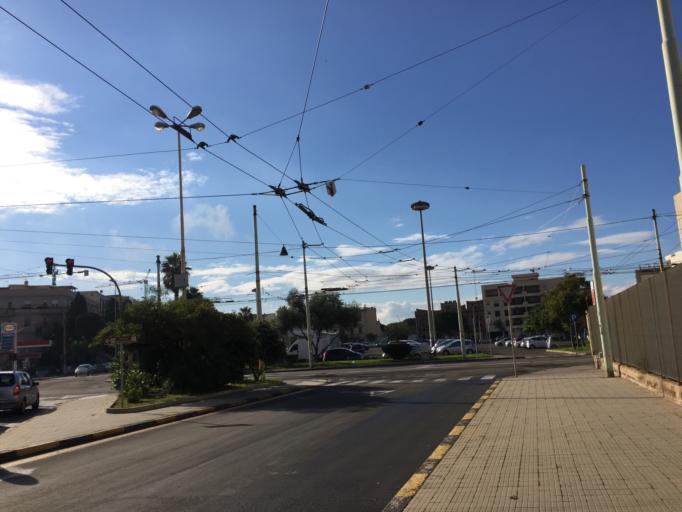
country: IT
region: Sardinia
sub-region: Provincia di Cagliari
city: Cagliari
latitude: 39.2103
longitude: 9.1229
